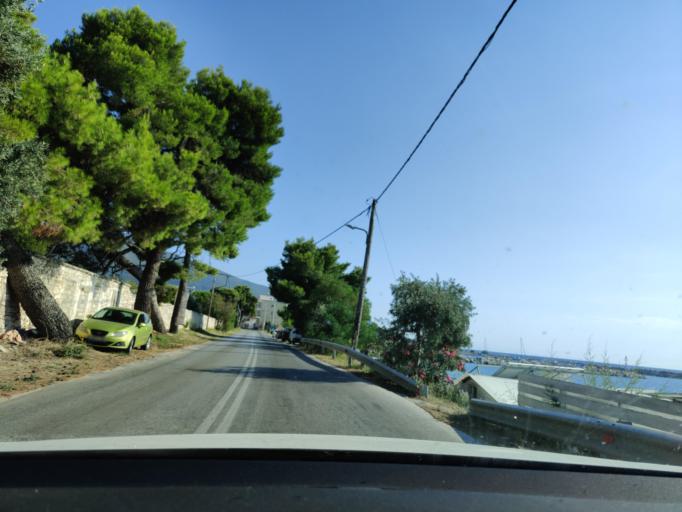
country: GR
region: East Macedonia and Thrace
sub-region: Nomos Kavalas
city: Prinos
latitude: 40.7121
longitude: 24.5340
